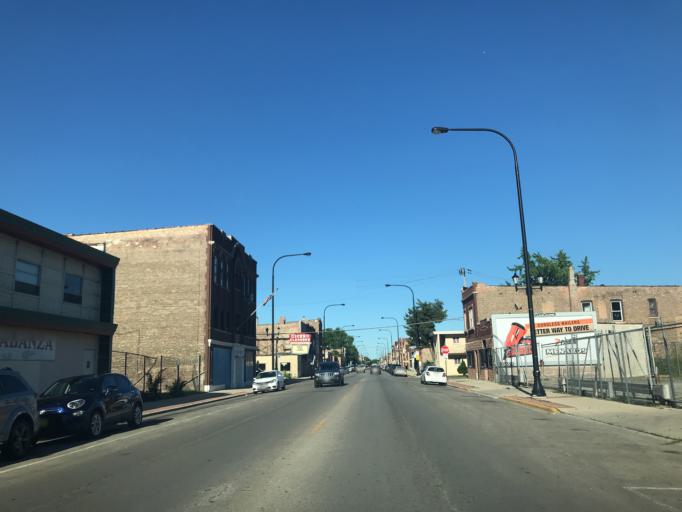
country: US
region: Illinois
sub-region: Cook County
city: Cicero
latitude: 41.8455
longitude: -87.7622
